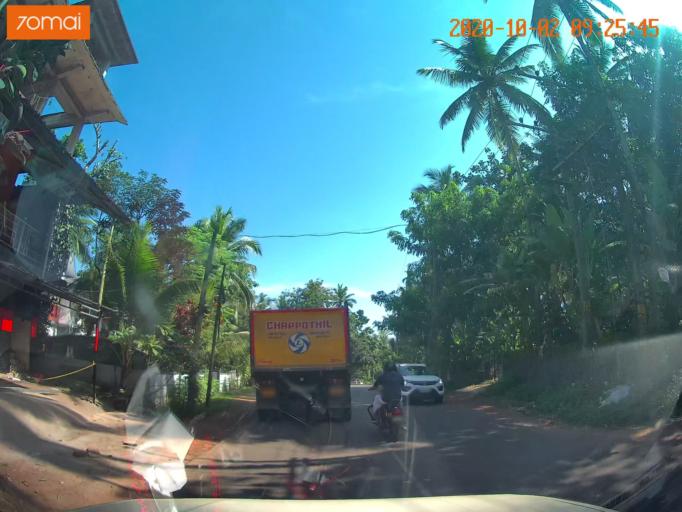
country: IN
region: Kerala
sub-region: Kozhikode
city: Naduvannur
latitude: 11.5893
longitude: 75.7660
